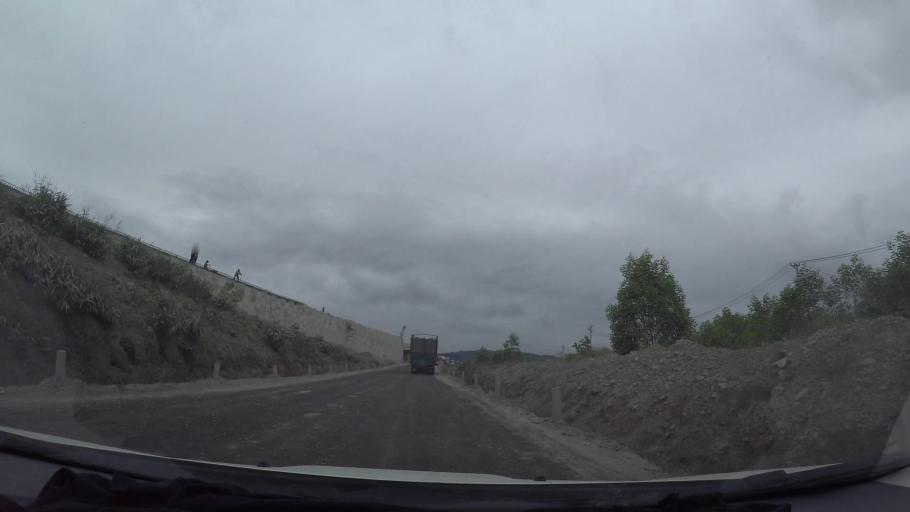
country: VN
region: Da Nang
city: Lien Chieu
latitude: 16.0954
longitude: 108.0883
